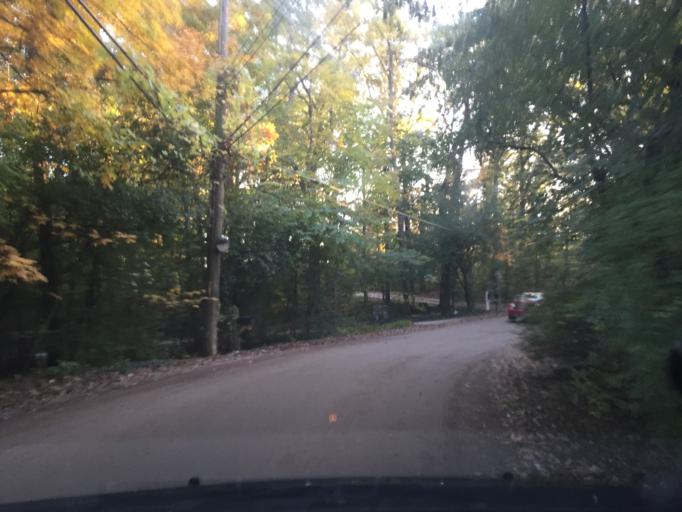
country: US
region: Michigan
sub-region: Oakland County
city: Bloomfield Hills
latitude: 42.5790
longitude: -83.2905
